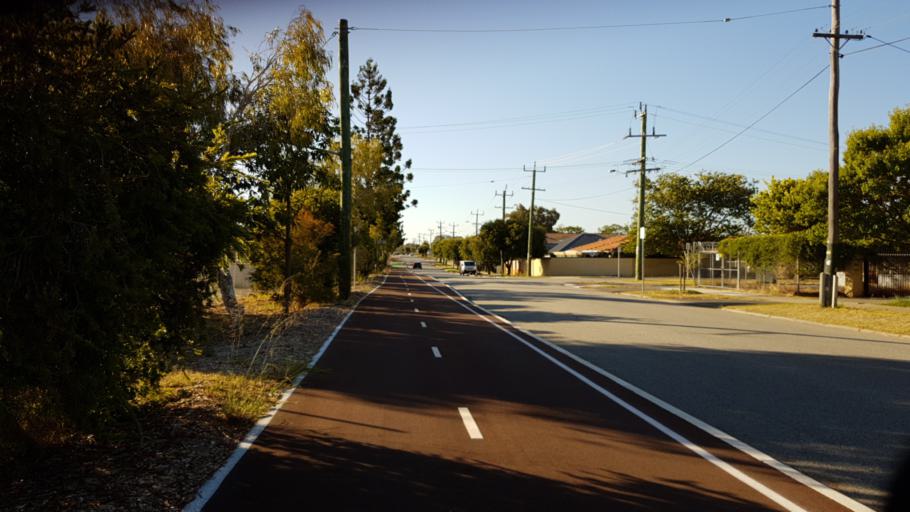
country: AU
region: Western Australia
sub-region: Victoria Park
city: Victoria Park
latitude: -31.9827
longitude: 115.9132
